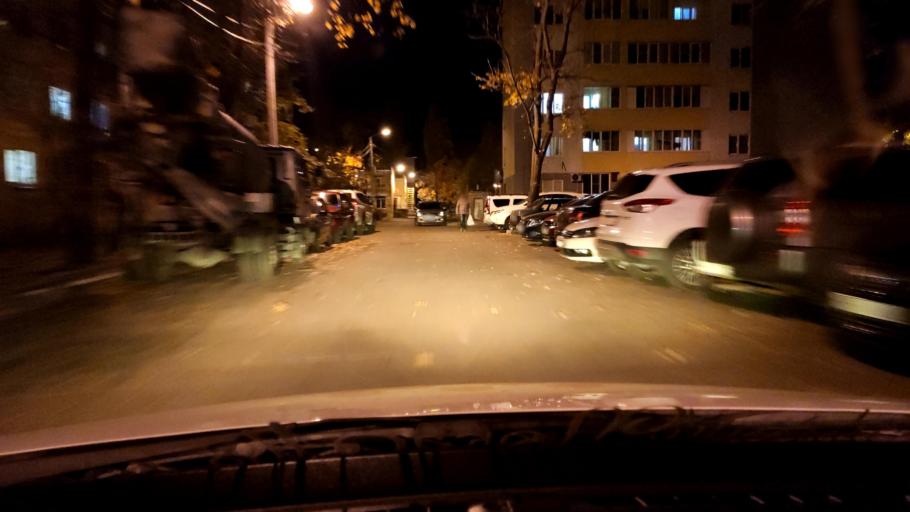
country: RU
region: Voronezj
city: Voronezh
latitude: 51.6502
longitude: 39.1558
